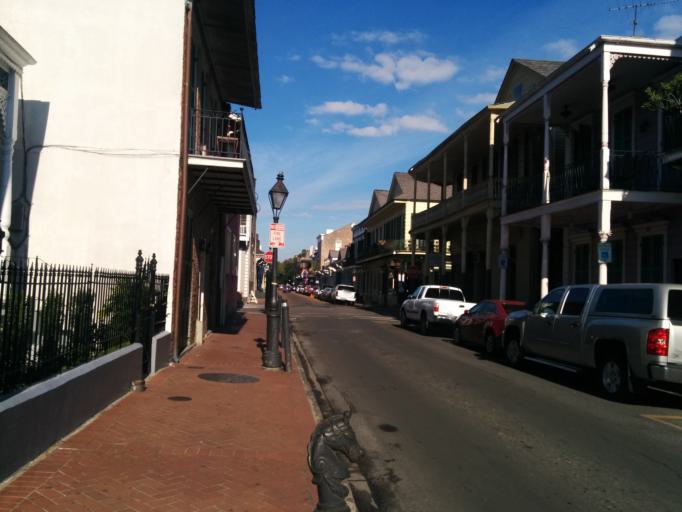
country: US
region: Louisiana
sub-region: Orleans Parish
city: New Orleans
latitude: 29.9590
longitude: -90.0662
